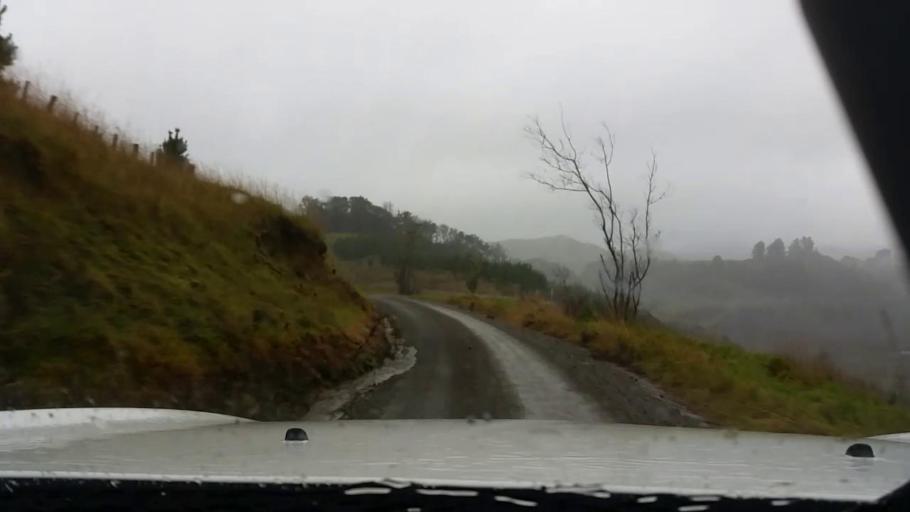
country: NZ
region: Wellington
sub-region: Masterton District
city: Masterton
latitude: -41.1993
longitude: 175.8112
